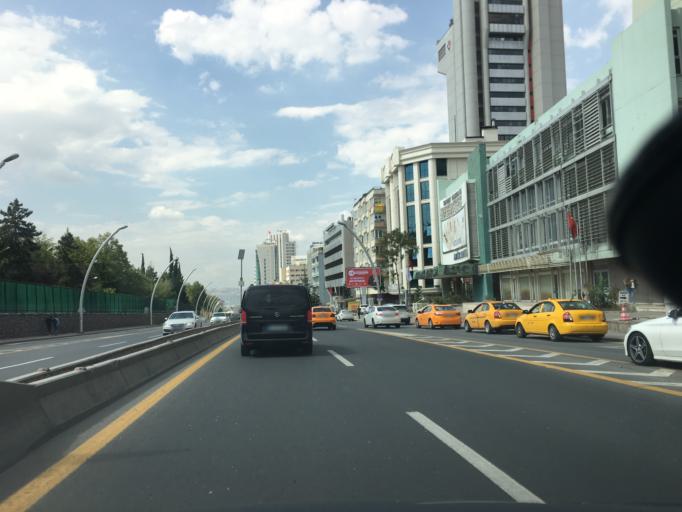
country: TR
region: Ankara
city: Cankaya
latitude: 39.9035
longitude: 32.8588
